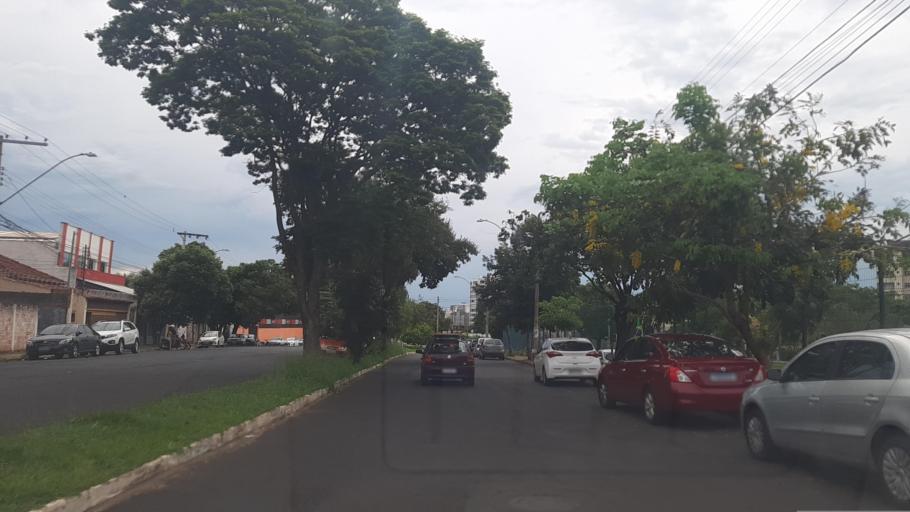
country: BR
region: Minas Gerais
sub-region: Uberlandia
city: Uberlandia
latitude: -18.9208
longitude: -48.2612
